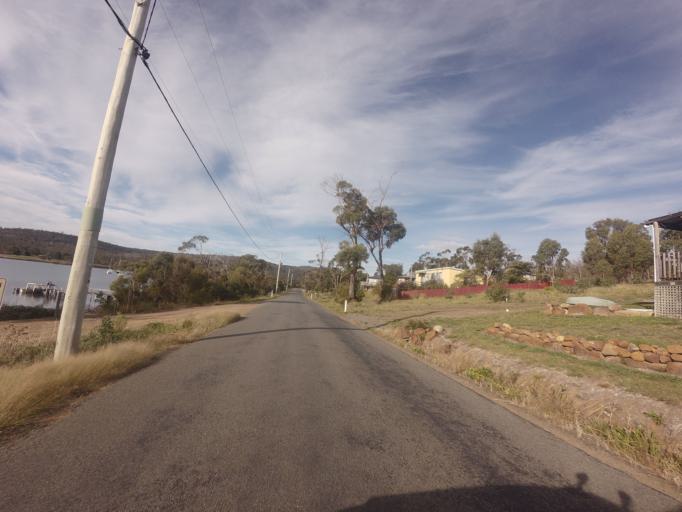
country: AU
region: Tasmania
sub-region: Sorell
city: Sorell
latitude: -42.9462
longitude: 147.8552
